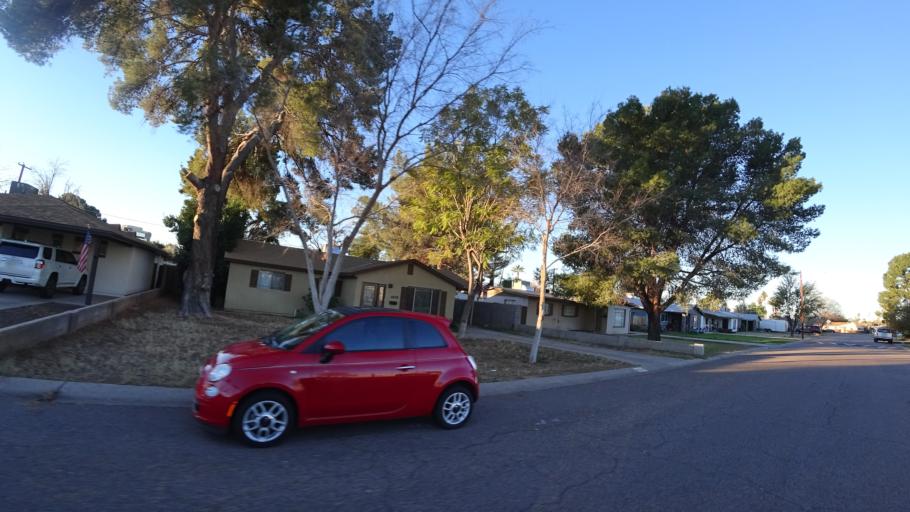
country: US
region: Arizona
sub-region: Maricopa County
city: Paradise Valley
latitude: 33.4844
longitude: -111.9893
